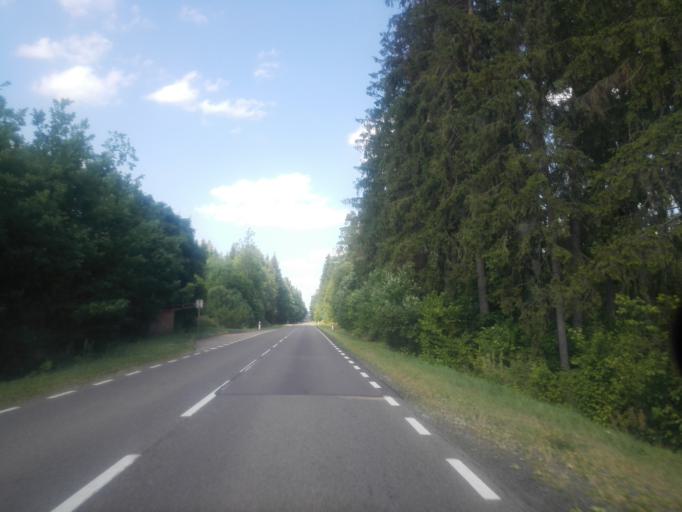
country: PL
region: Podlasie
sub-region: Powiat sejnenski
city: Sejny
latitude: 54.0152
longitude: 23.3343
